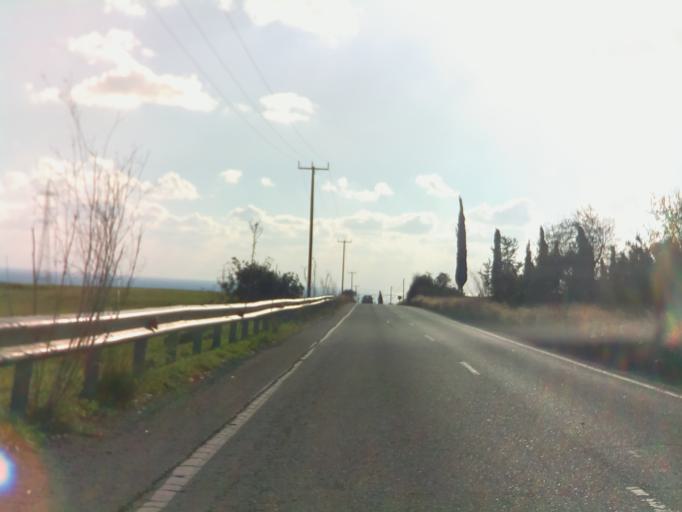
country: CY
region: Pafos
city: Mesogi
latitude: 34.7523
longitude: 32.5168
